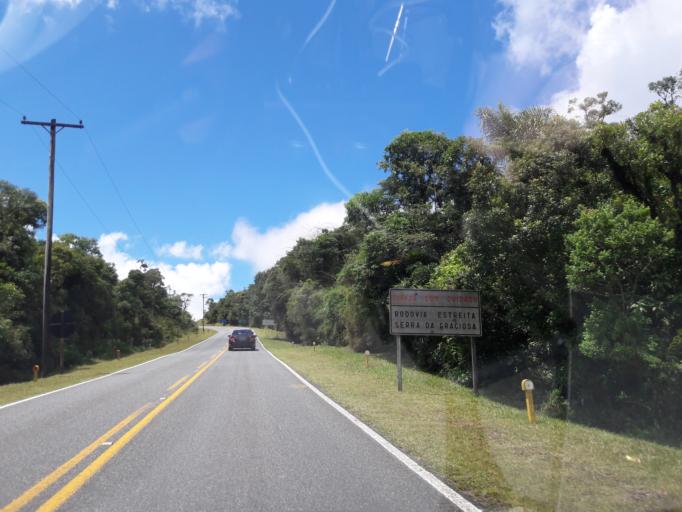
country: BR
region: Parana
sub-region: Campina Grande Do Sul
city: Campina Grande do Sul
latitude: -25.3329
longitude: -48.9085
